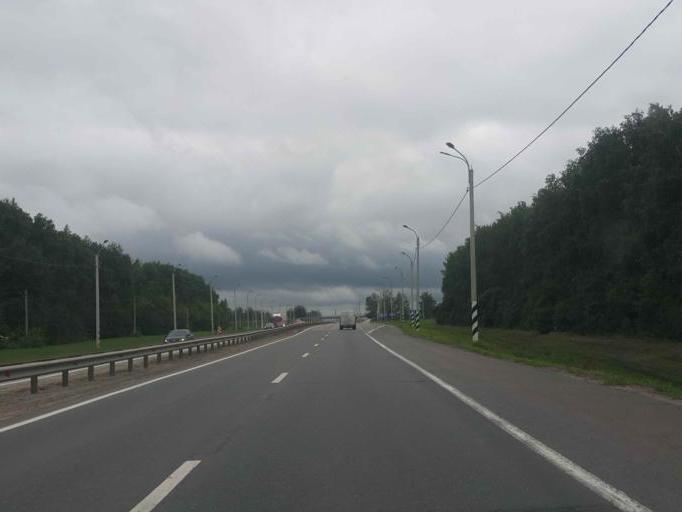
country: RU
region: Tambov
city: Komsomolets
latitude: 52.7368
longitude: 41.2603
